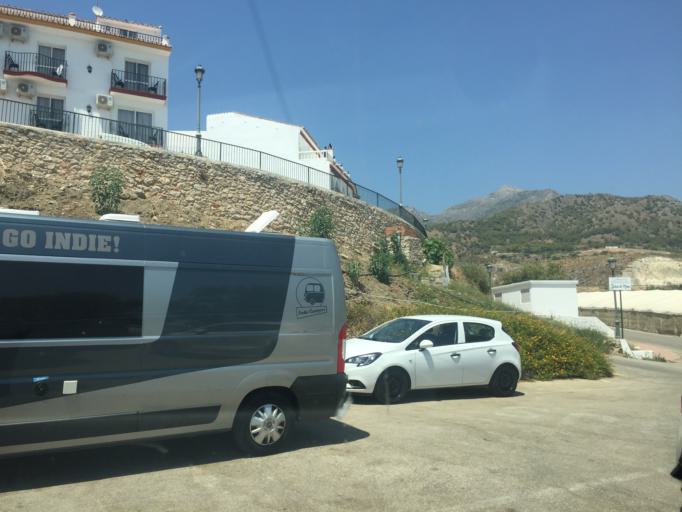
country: ES
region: Andalusia
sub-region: Provincia de Malaga
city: Nerja
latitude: 36.7572
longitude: -3.8423
